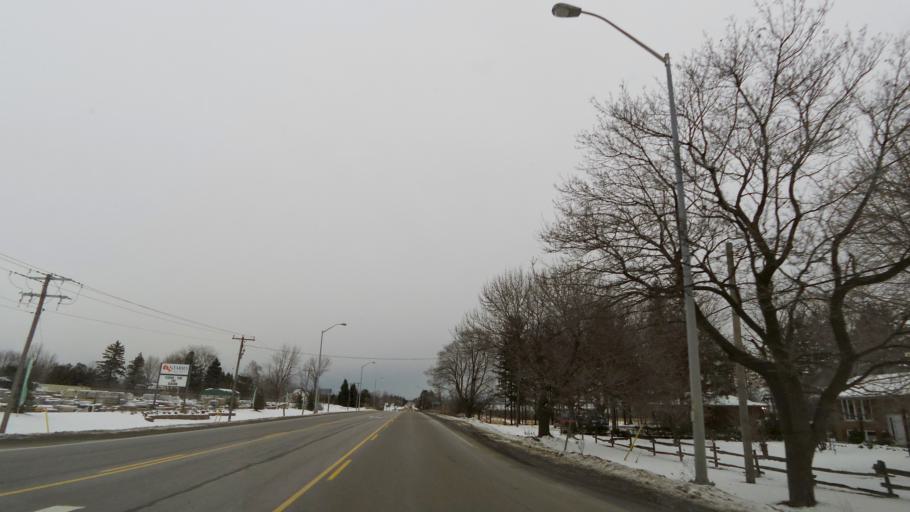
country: CA
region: Ontario
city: Ancaster
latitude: 43.2961
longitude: -79.9792
